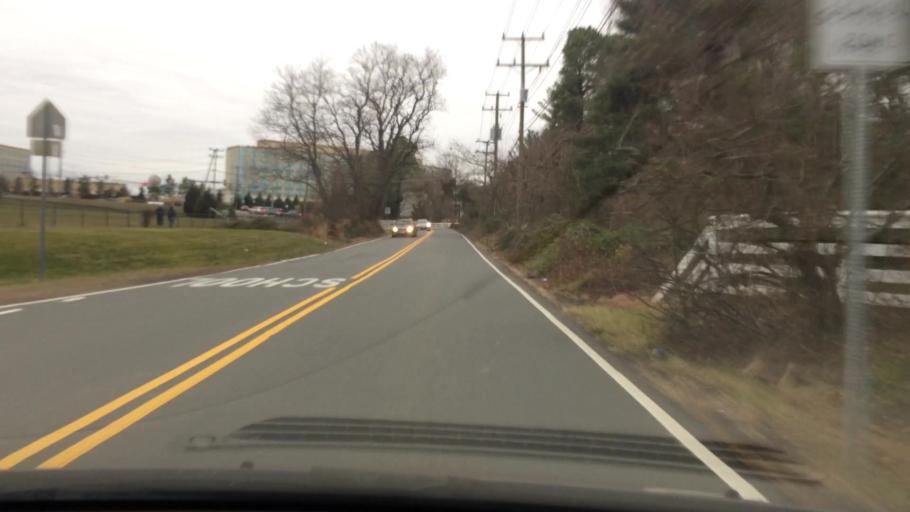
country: US
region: Virginia
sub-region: Fairfax County
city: Chantilly
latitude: 38.9094
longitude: -77.4200
